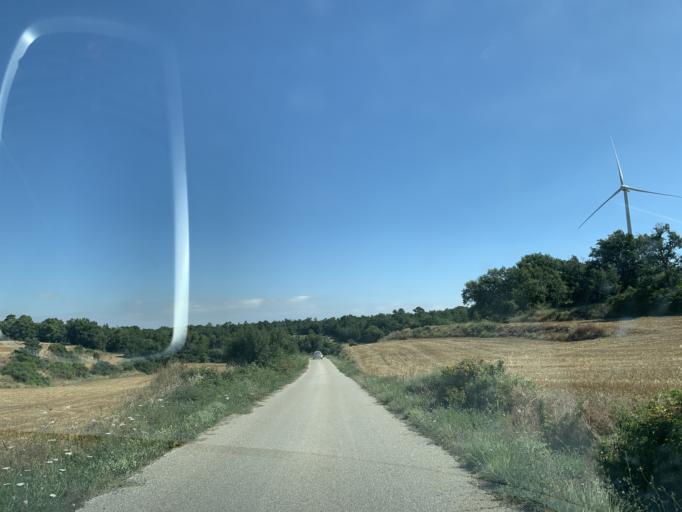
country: ES
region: Catalonia
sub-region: Provincia de Tarragona
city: Conesa
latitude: 41.5381
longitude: 1.2841
